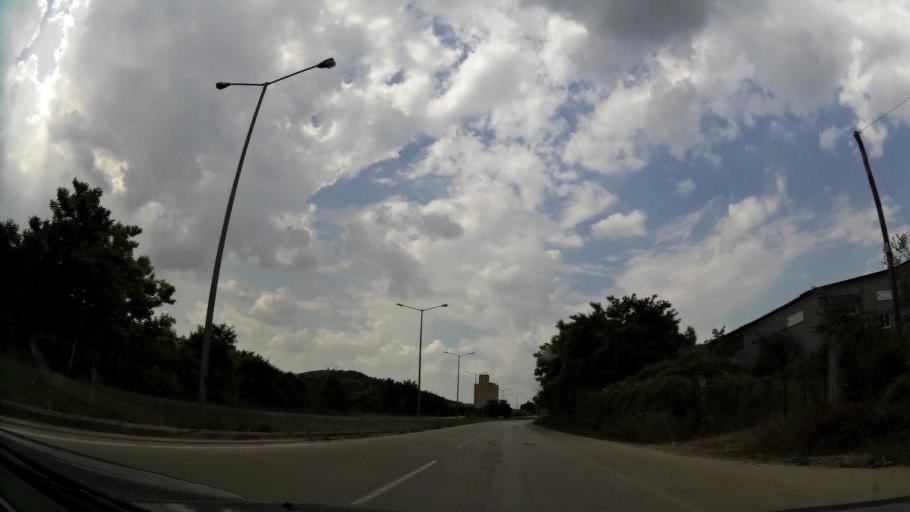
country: GR
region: West Macedonia
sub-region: Nomos Kozanis
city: Koila
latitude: 40.3388
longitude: 21.8248
